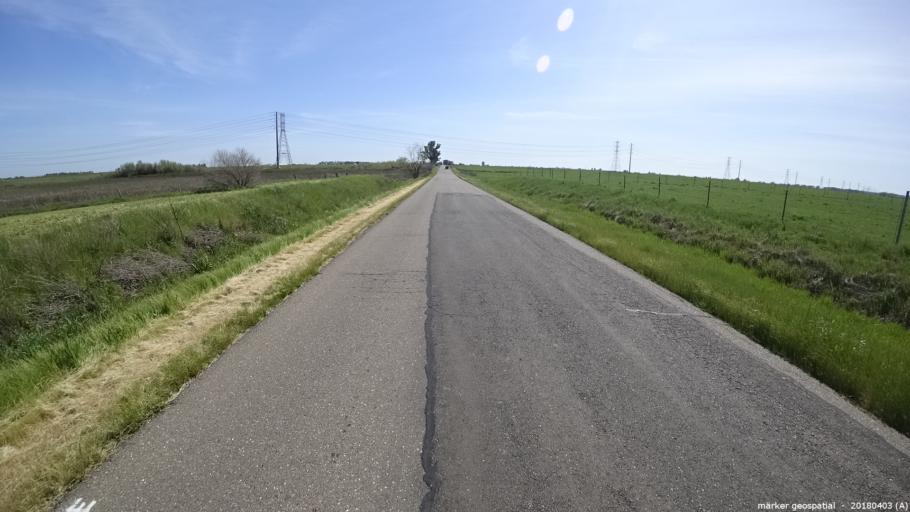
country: US
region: California
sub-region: Sacramento County
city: Wilton
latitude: 38.3541
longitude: -121.2976
